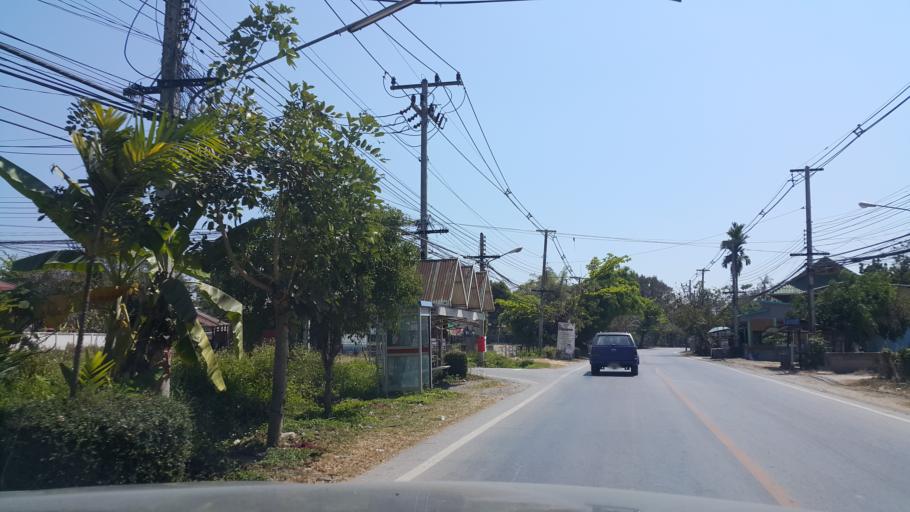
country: TH
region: Chiang Mai
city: San Sai
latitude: 18.8669
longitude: 99.0520
